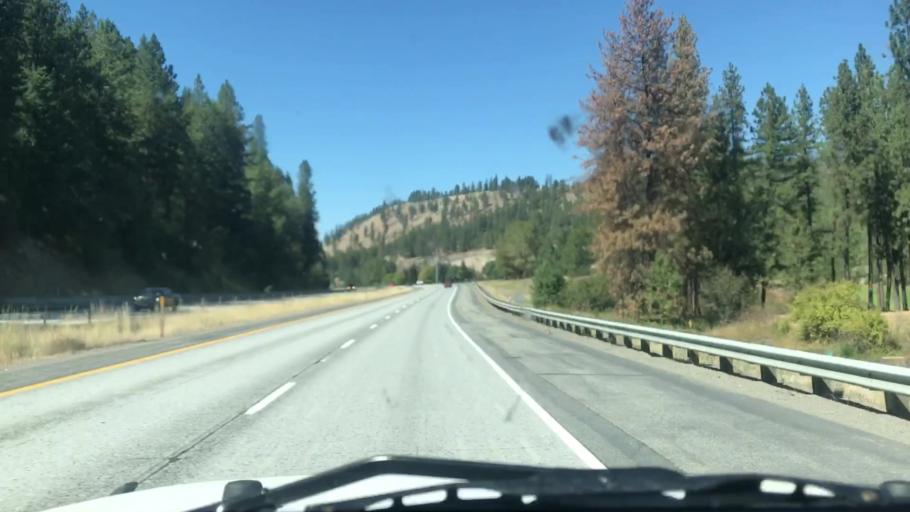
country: US
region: Washington
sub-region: Spokane County
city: Spokane
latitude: 47.6073
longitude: -117.4158
